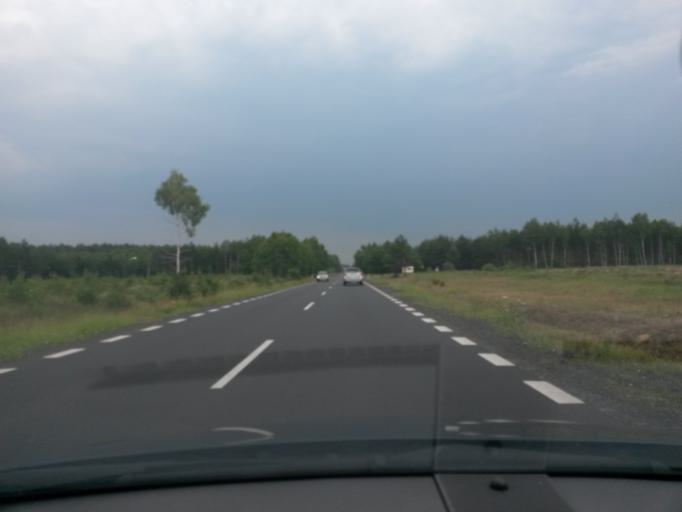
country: PL
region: Silesian Voivodeship
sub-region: Powiat czestochowski
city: Olsztyn
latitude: 50.7600
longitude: 19.2111
